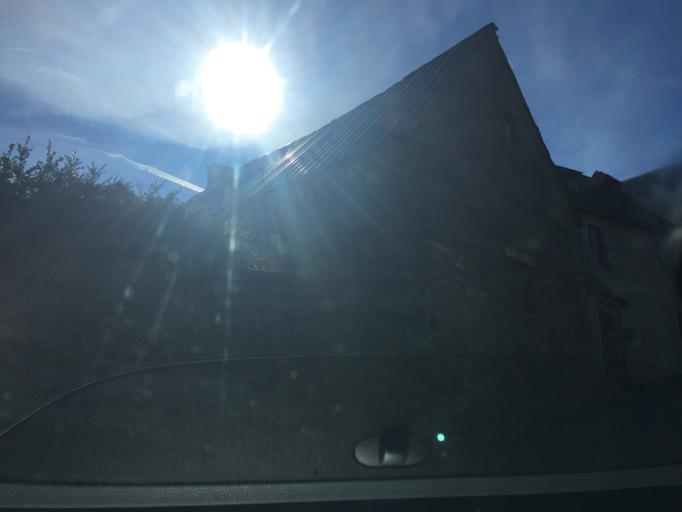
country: FR
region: Midi-Pyrenees
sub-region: Departement des Hautes-Pyrenees
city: Saint-Lary-Soulan
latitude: 42.8117
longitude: 0.3516
